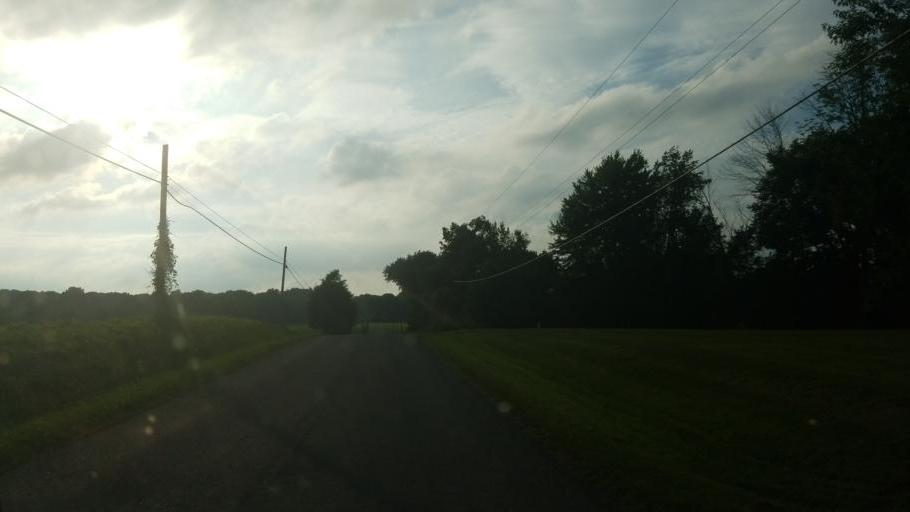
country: US
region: Ohio
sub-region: Wayne County
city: Wooster
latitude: 40.8040
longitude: -82.0529
